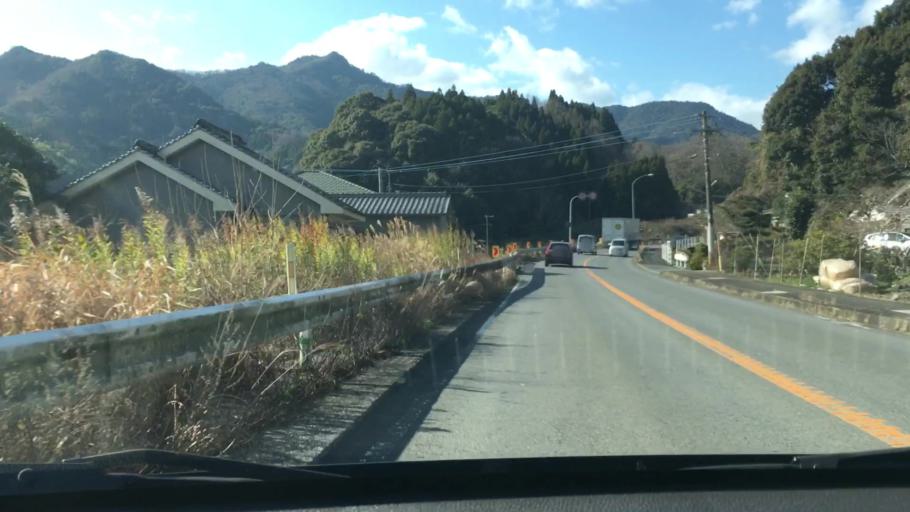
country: JP
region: Oita
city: Saiki
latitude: 32.9892
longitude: 131.8346
